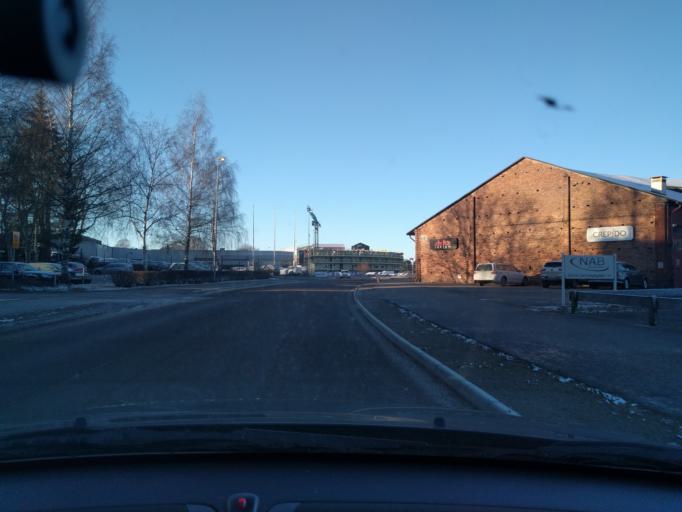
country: SE
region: Kronoberg
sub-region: Vaxjo Kommun
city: Vaexjoe
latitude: 56.8760
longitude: 14.7945
